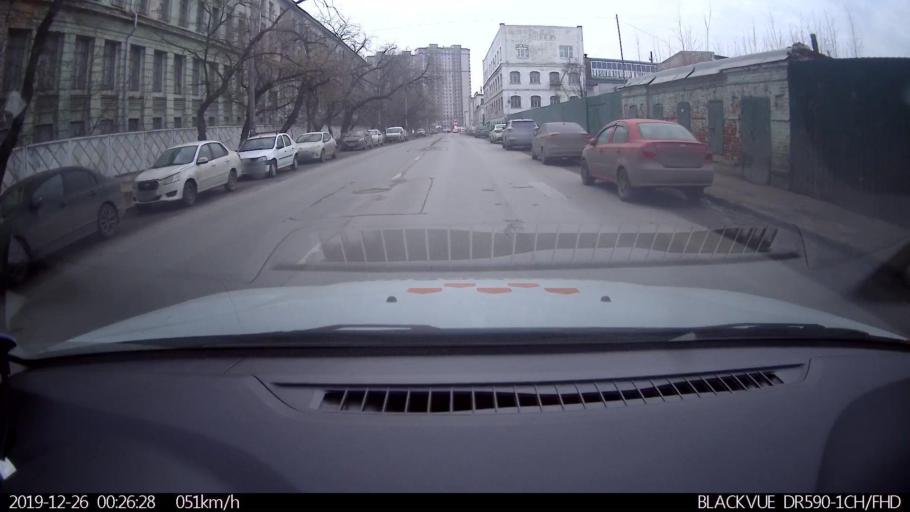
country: RU
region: Nizjnij Novgorod
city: Nizhniy Novgorod
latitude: 56.3121
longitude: 43.9493
